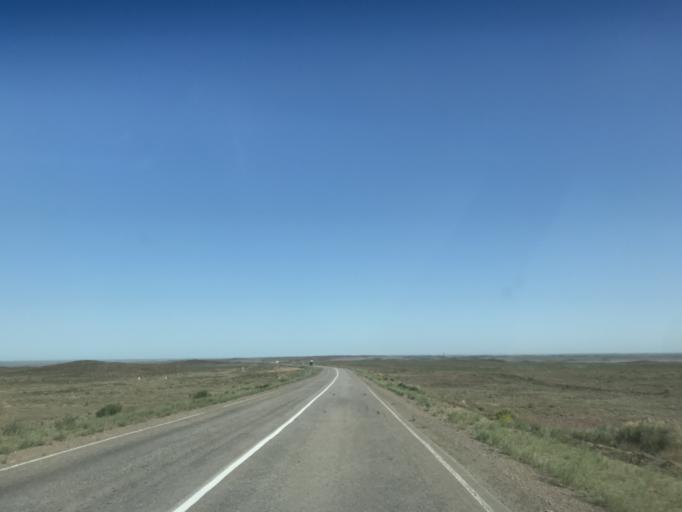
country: KZ
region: Zhambyl
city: Mynaral
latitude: 45.4719
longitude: 73.5554
